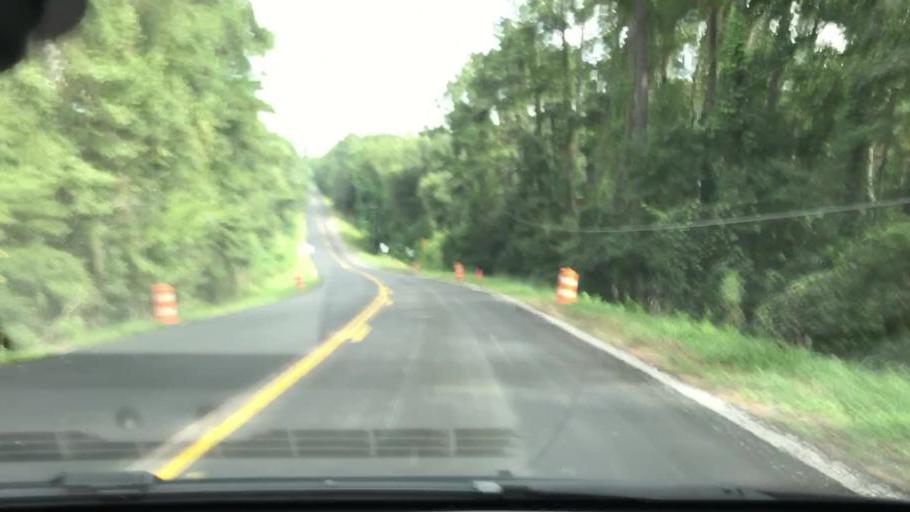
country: US
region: Georgia
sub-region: Clay County
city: Fort Gaines
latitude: 31.5965
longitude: -85.0445
